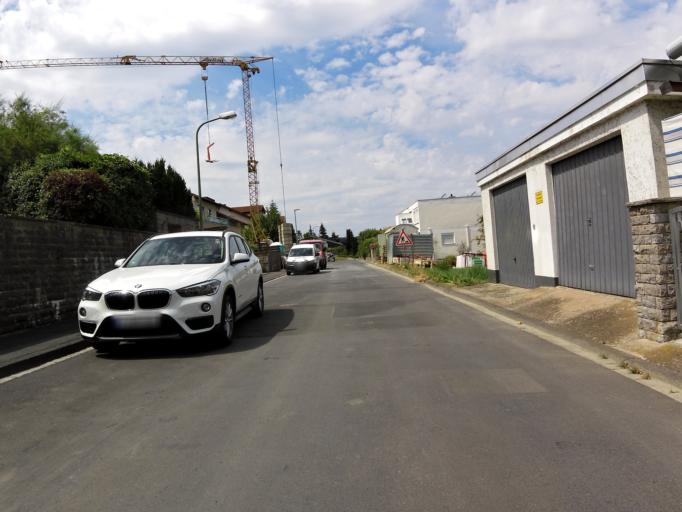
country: DE
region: Bavaria
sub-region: Regierungsbezirk Unterfranken
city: Randersacker
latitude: 49.7577
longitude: 9.9527
